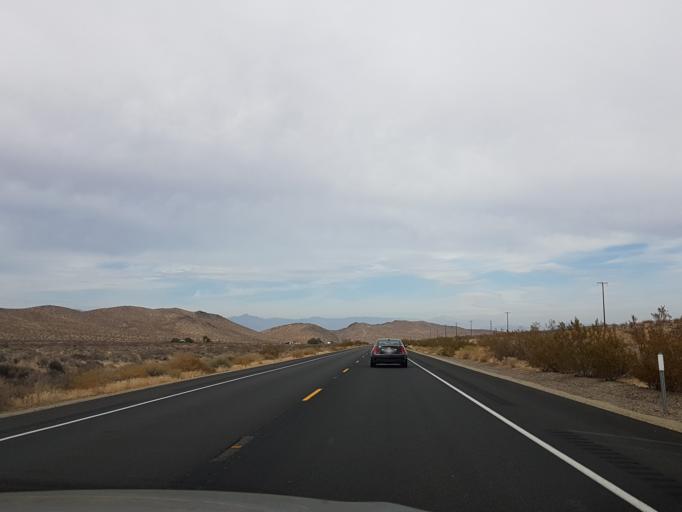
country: US
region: California
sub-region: Kern County
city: Ridgecrest
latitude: 35.5273
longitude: -117.6779
